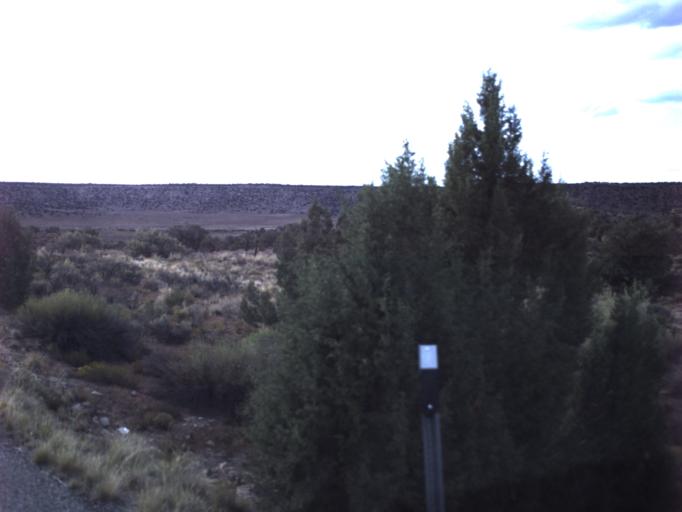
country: US
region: Utah
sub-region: San Juan County
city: Blanding
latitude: 37.4341
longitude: -109.3956
